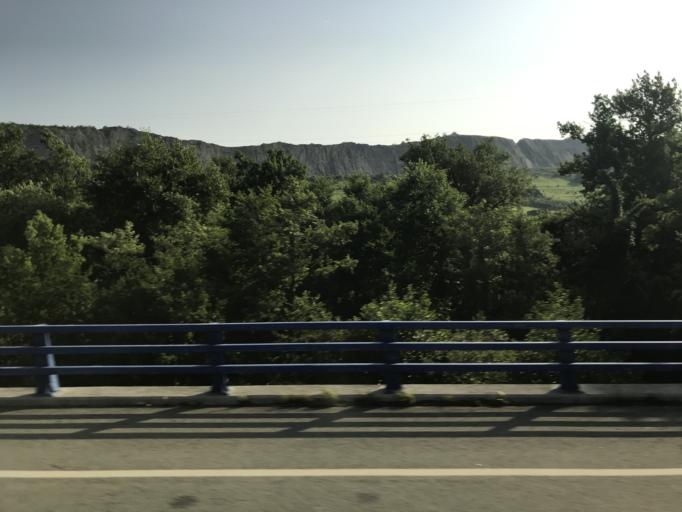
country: ES
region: Navarre
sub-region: Provincia de Navarra
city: Altsasu
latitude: 42.9197
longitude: -2.2042
